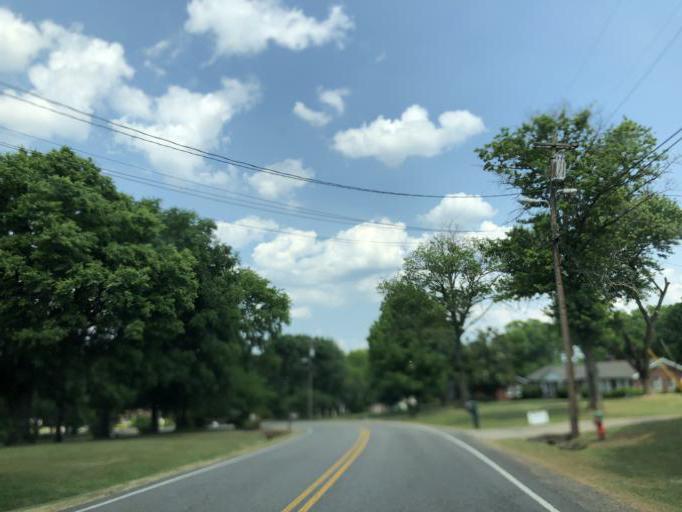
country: US
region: Tennessee
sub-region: Davidson County
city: Goodlettsville
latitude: 36.2443
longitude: -86.7277
